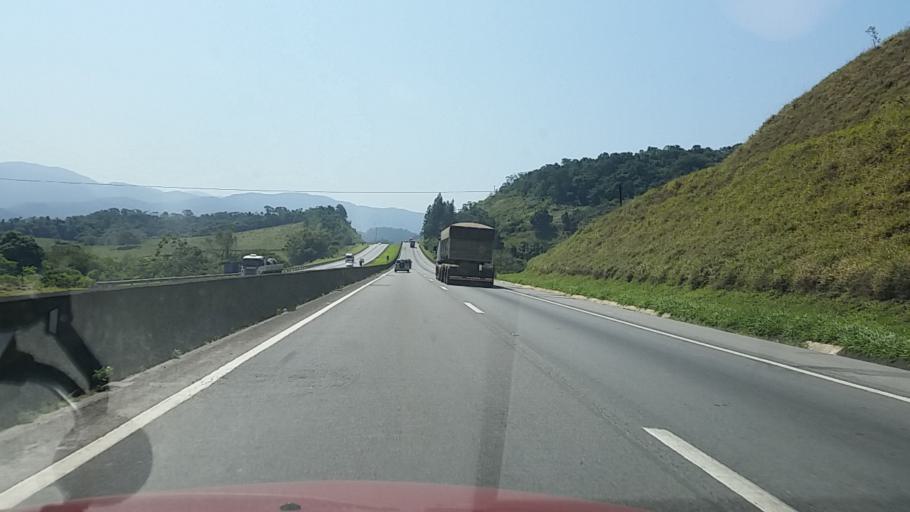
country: BR
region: Sao Paulo
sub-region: Miracatu
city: Miracatu
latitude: -24.1730
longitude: -47.3422
